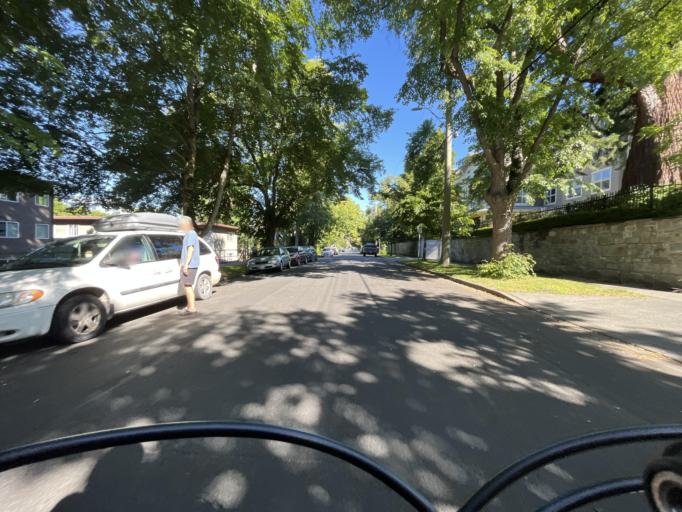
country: CA
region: British Columbia
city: Victoria
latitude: 48.4182
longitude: -123.3601
